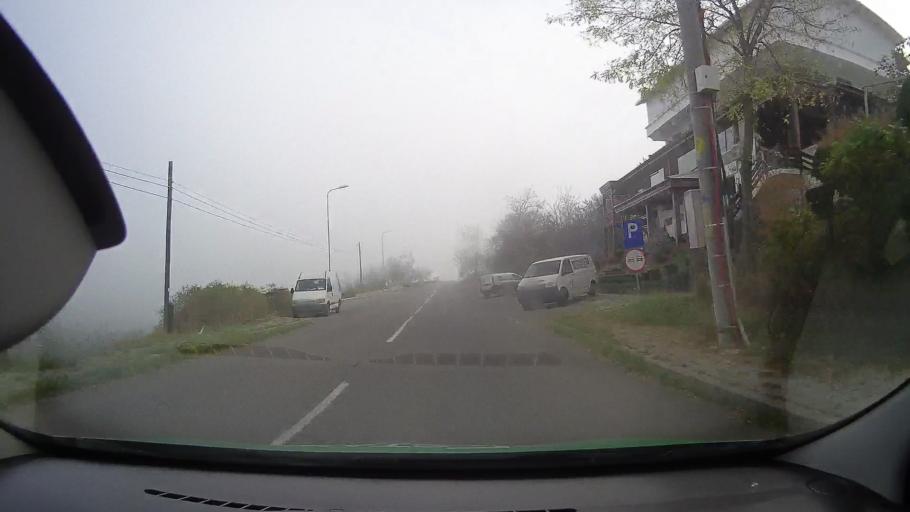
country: RO
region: Tulcea
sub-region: Municipiul Tulcea
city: Tulcea
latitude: 45.1668
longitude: 28.8314
